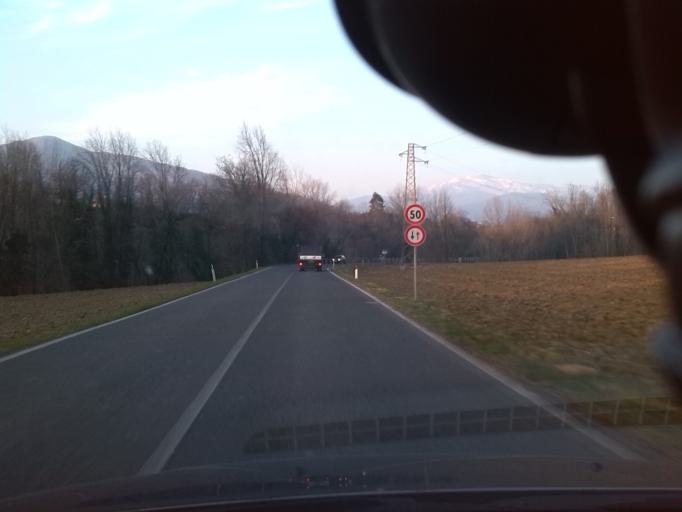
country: IT
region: Friuli Venezia Giulia
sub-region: Provincia di Udine
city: San Pietro al Natisone
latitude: 46.1082
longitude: 13.4744
